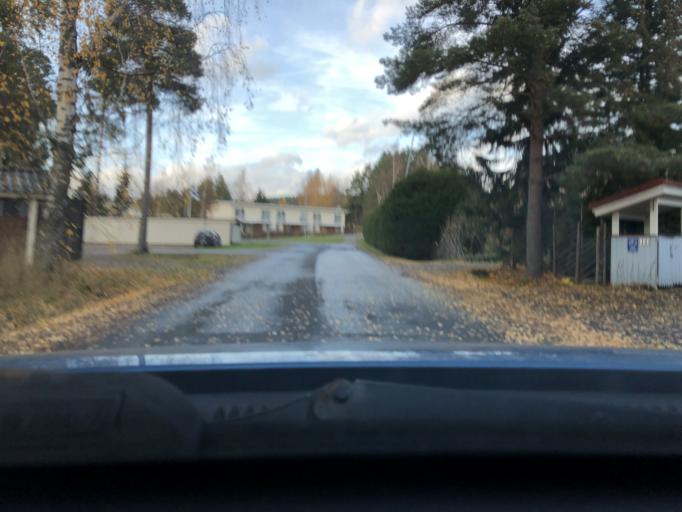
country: FI
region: Pirkanmaa
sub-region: Tampere
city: Kangasala
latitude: 61.4693
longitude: 24.0300
